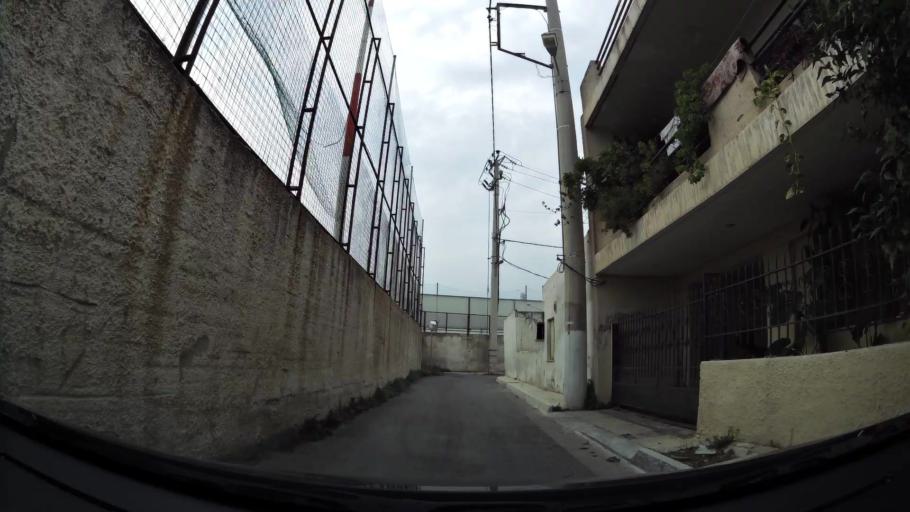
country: GR
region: Attica
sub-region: Nomarchia Athinas
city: Tavros
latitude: 37.9704
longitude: 23.6846
